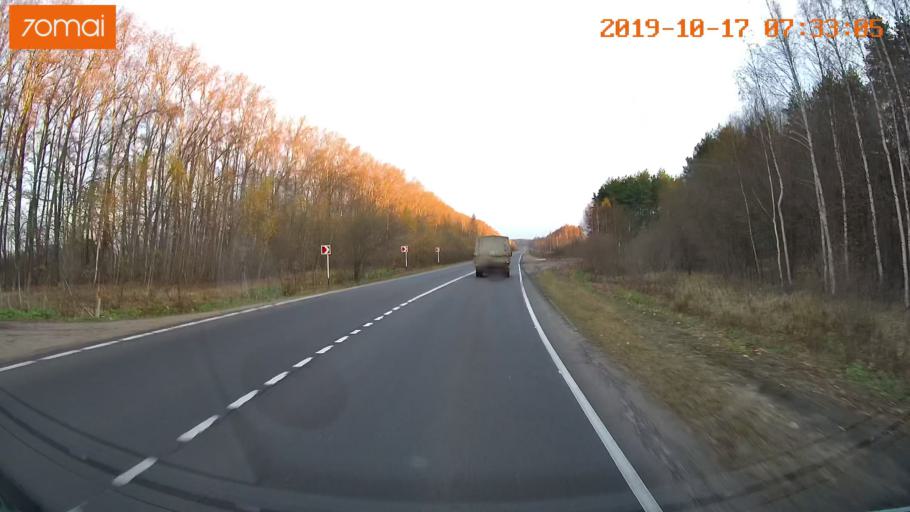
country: RU
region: Ivanovo
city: Gavrilov Posad
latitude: 56.4017
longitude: 39.9621
